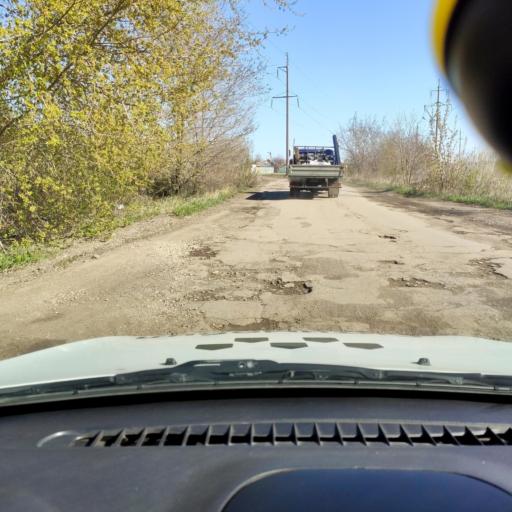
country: RU
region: Samara
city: Tol'yatti
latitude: 53.5804
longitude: 49.2935
